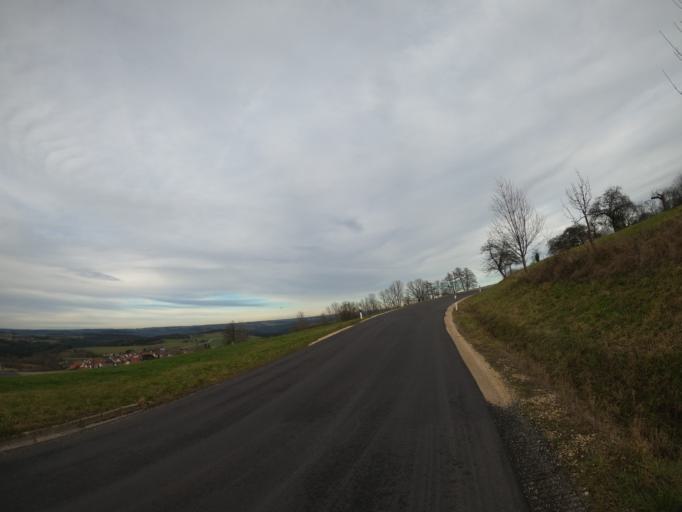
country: DE
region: Baden-Wuerttemberg
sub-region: Regierungsbezirk Stuttgart
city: Ottenbach
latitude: 48.7513
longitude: 9.7216
